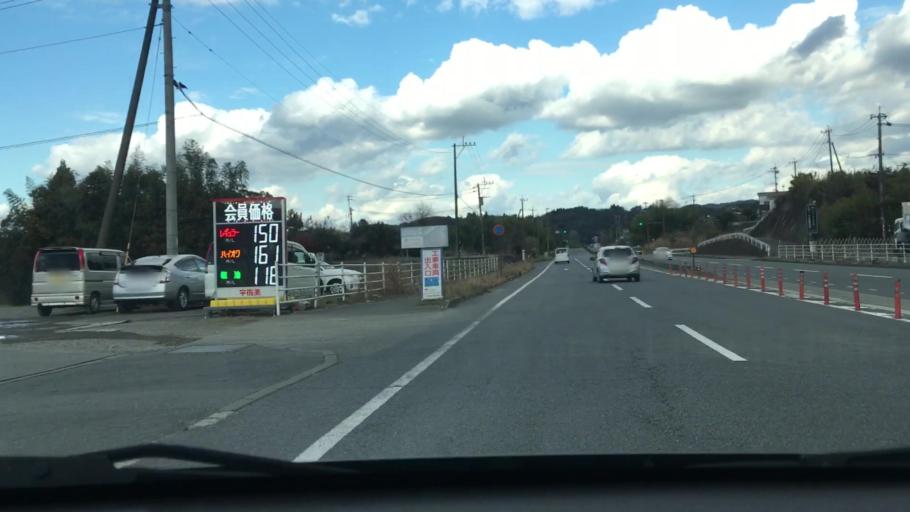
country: JP
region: Oita
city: Oita
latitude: 33.1255
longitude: 131.6554
